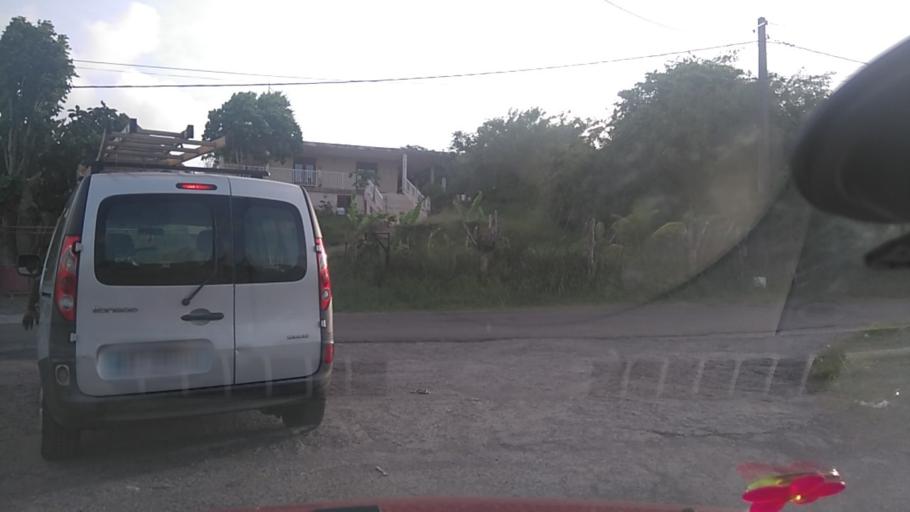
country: MQ
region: Martinique
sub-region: Martinique
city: Le Marin
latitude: 14.4568
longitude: -60.8406
